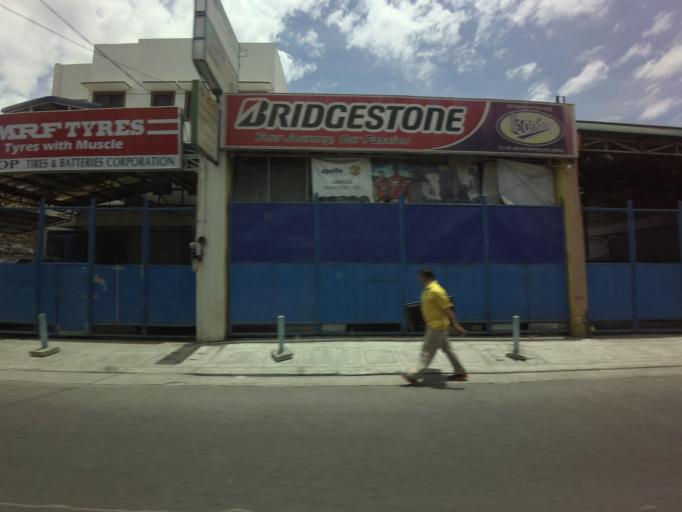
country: PH
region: Metro Manila
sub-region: Marikina
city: Calumpang
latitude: 14.6032
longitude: 121.0993
